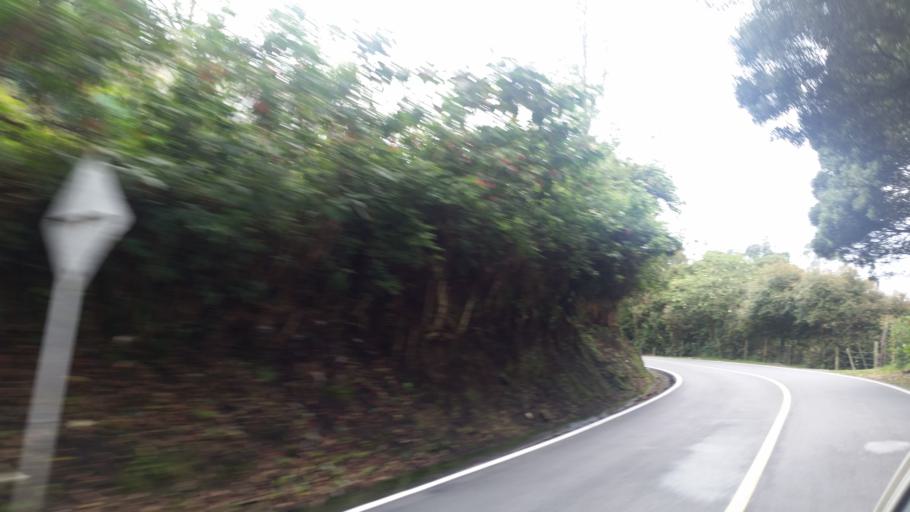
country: CO
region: Cundinamarca
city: Choachi
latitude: 4.5577
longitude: -73.9359
